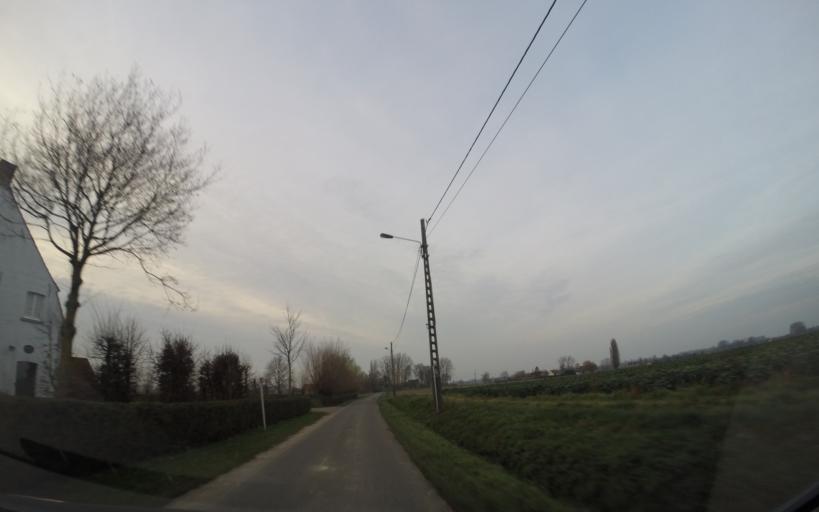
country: BE
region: Flanders
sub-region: Provincie West-Vlaanderen
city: Ruiselede
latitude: 51.0211
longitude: 3.4151
